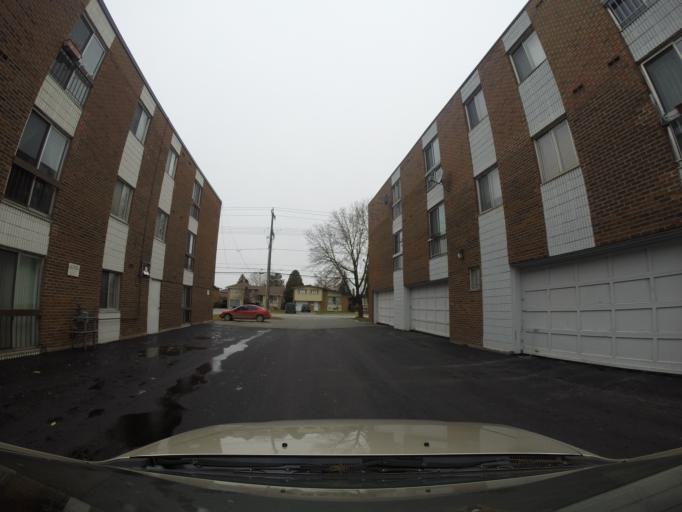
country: CA
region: Ontario
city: Greater Sudbury
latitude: 46.4614
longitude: -81.0275
